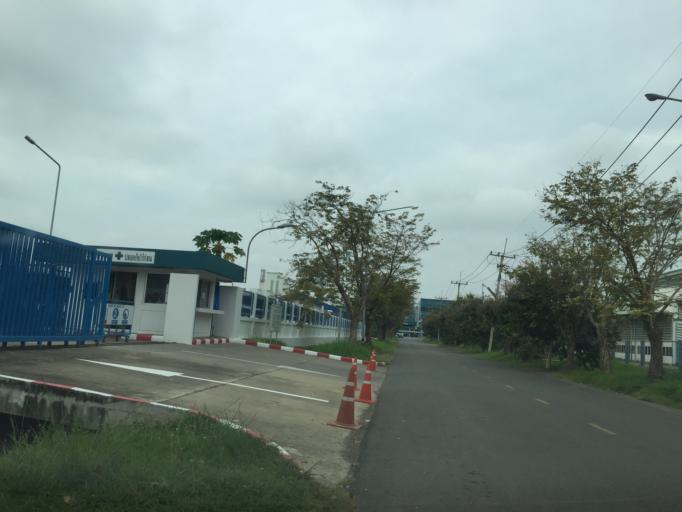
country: TH
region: Lamphun
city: Lamphun
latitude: 18.5953
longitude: 99.0488
